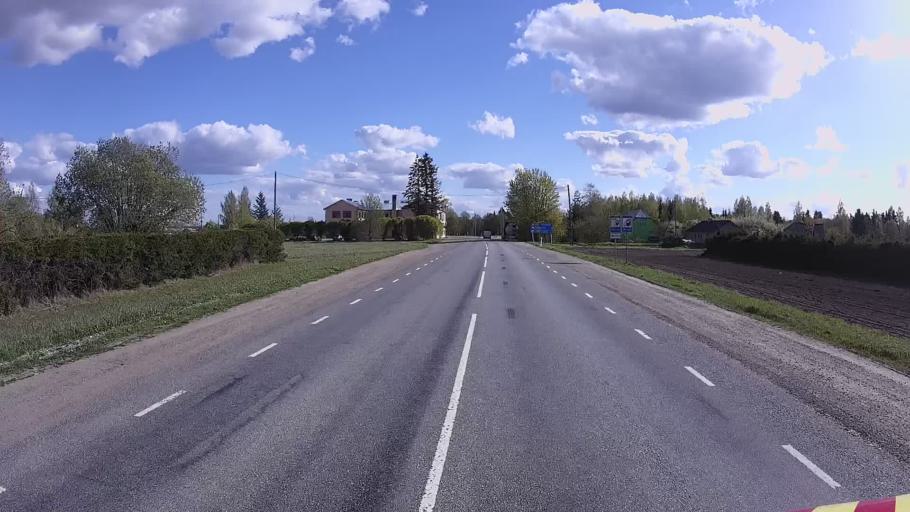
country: EE
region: Jogevamaa
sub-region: Poltsamaa linn
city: Poltsamaa
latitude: 58.6653
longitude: 25.9908
